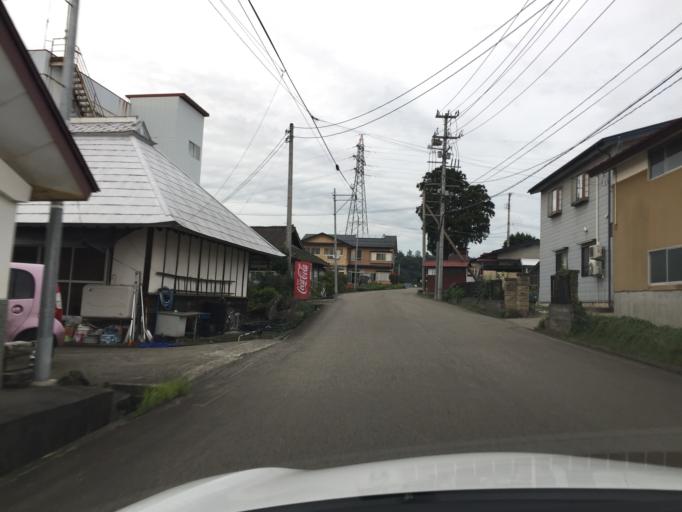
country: JP
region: Fukushima
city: Kitakata
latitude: 37.5743
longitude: 139.9251
